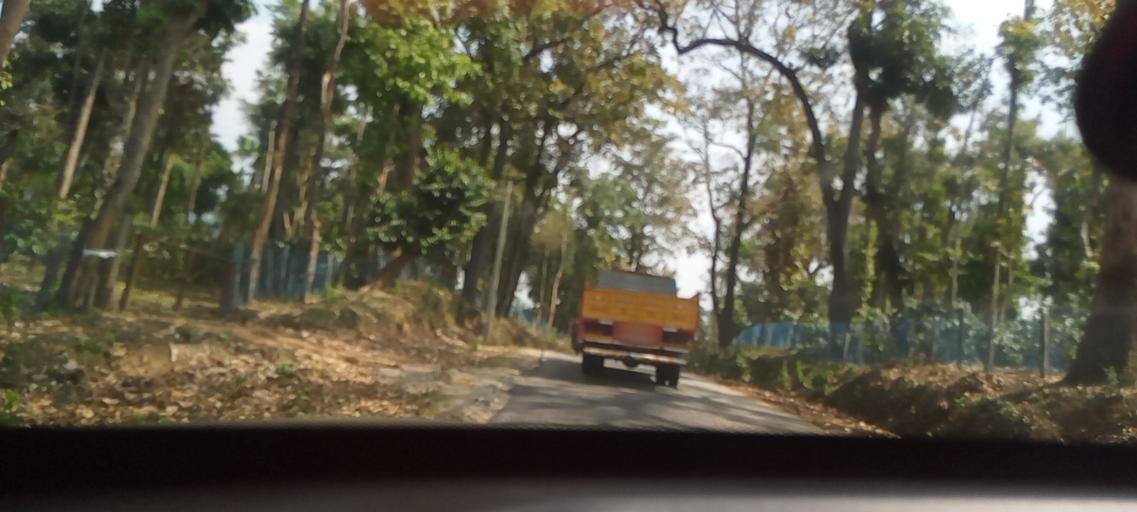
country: IN
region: Karnataka
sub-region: Chikmagalur
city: Mudigere
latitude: 13.3158
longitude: 75.5701
